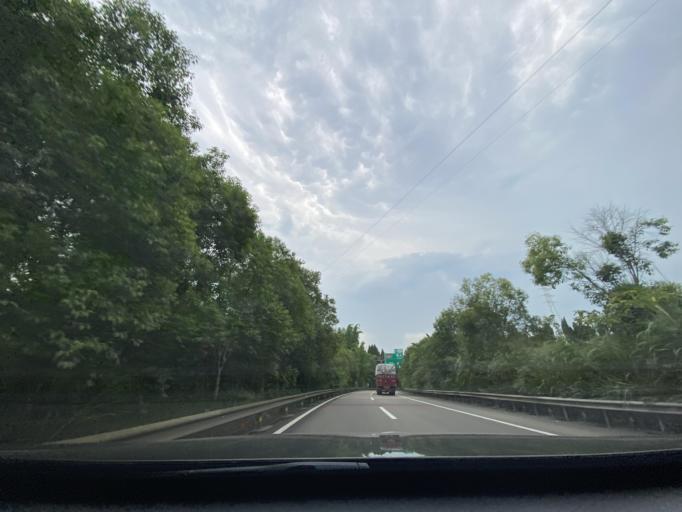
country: CN
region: Sichuan
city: Chonglong
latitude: 29.6807
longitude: 104.9556
